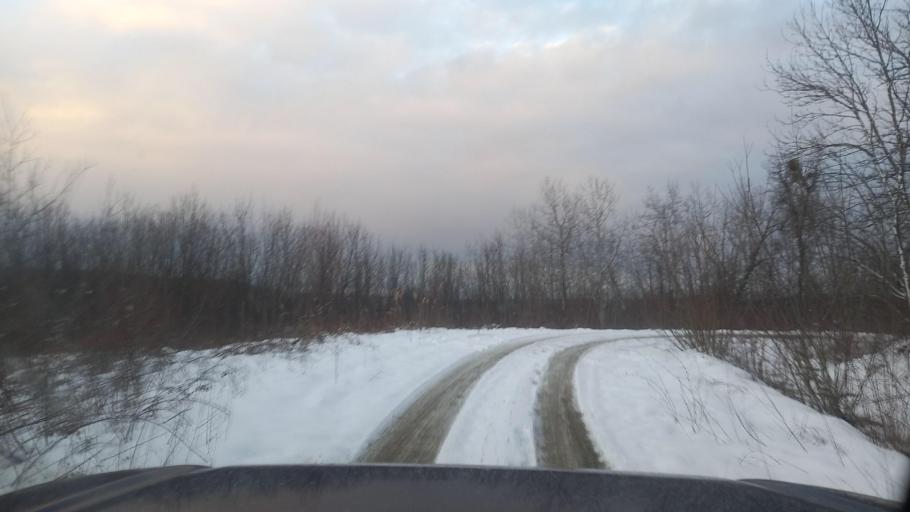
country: RU
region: Krasnodarskiy
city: Smolenskaya
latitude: 44.6723
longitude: 38.7917
